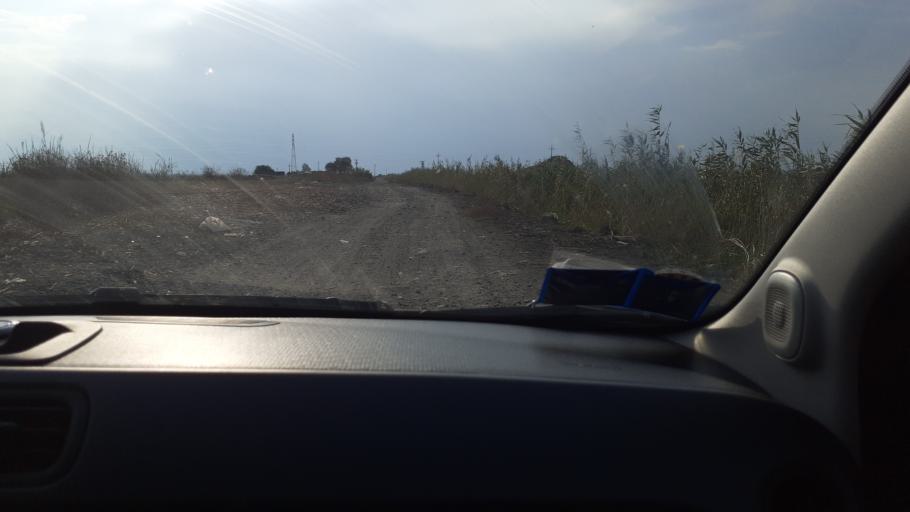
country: IT
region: Sicily
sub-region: Catania
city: Catania
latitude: 37.4332
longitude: 15.0107
